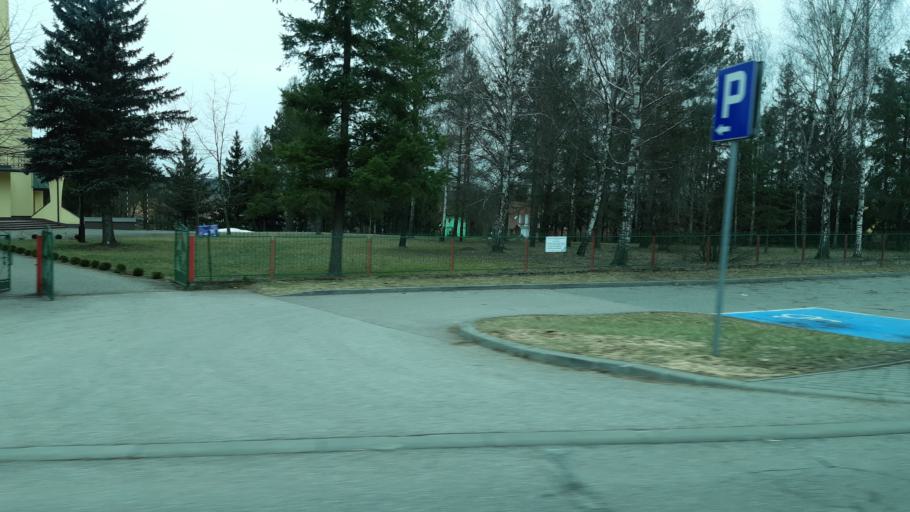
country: PL
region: Podlasie
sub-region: Suwalki
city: Suwalki
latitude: 54.3220
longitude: 22.9713
